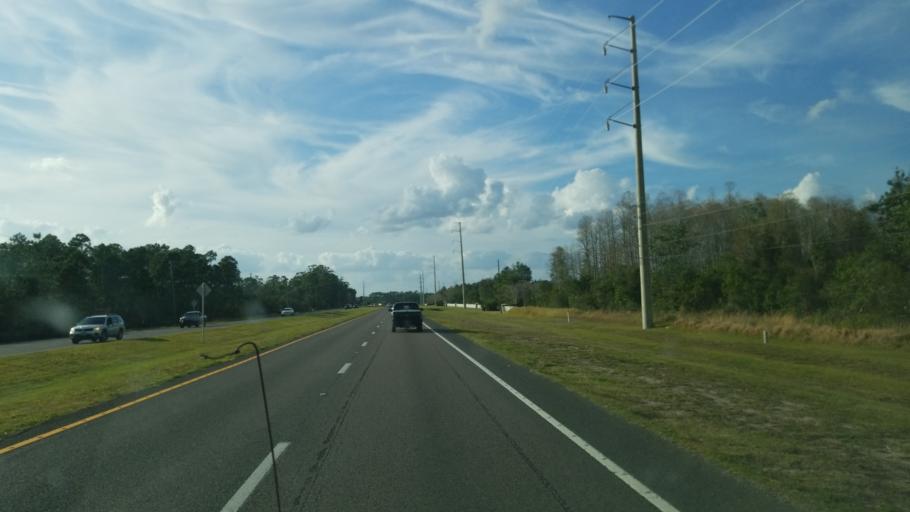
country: US
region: Florida
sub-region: Osceola County
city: Saint Cloud
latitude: 28.1925
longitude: -81.1556
